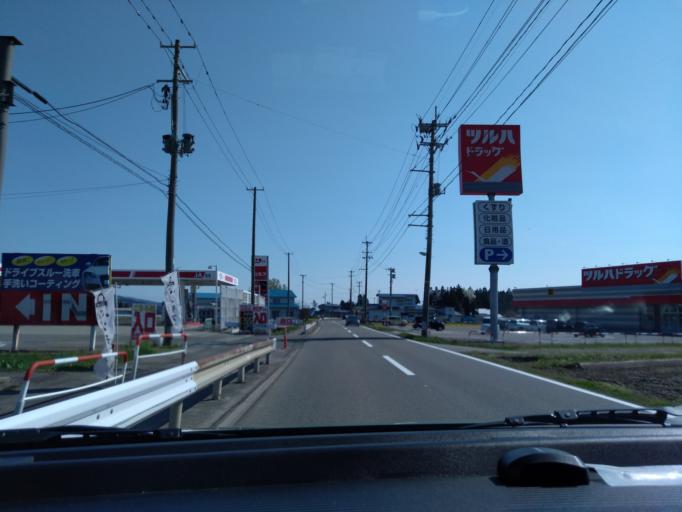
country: JP
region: Akita
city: Omagari
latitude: 39.4600
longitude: 140.5800
